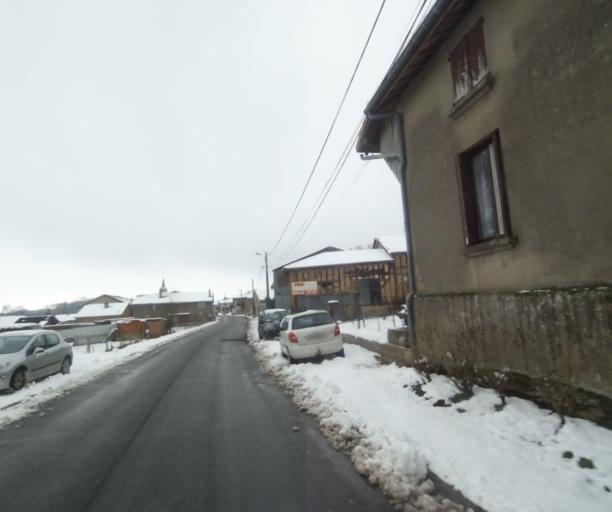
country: FR
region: Champagne-Ardenne
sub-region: Departement de la Haute-Marne
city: Laneuville-a-Remy
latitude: 48.4613
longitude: 4.8506
